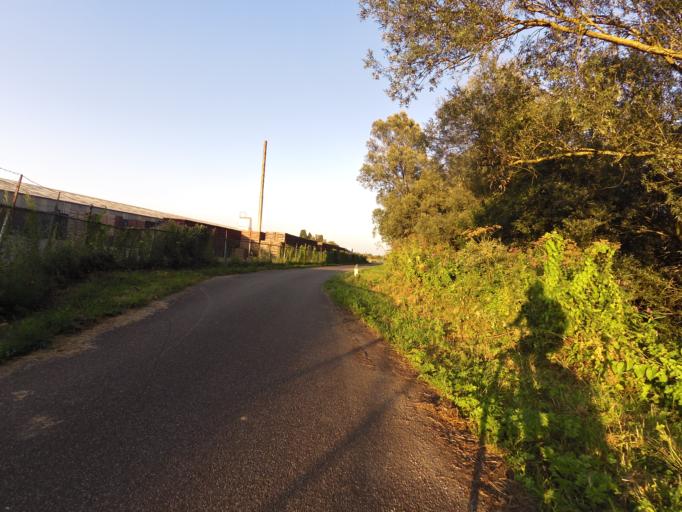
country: NL
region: Gelderland
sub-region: Gemeente Zevenaar
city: Zevenaar
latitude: 51.8733
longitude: 6.0557
